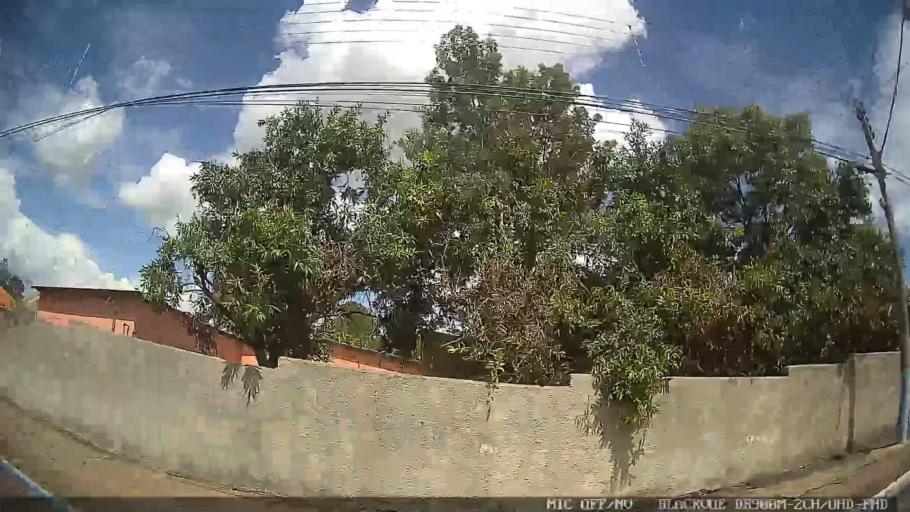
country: BR
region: Sao Paulo
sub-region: Conchas
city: Conchas
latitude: -23.0189
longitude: -48.0103
